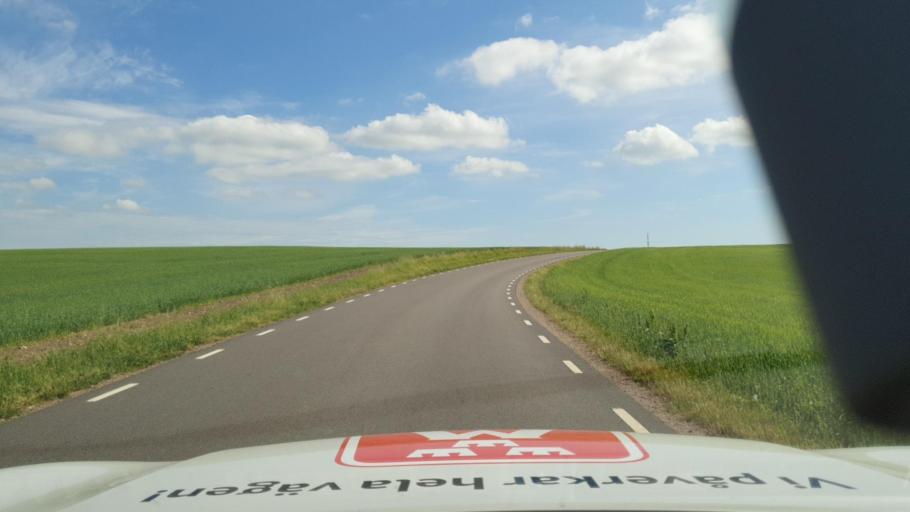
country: SE
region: Skane
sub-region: Sjobo Kommun
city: Blentarp
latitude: 55.5565
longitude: 13.5613
